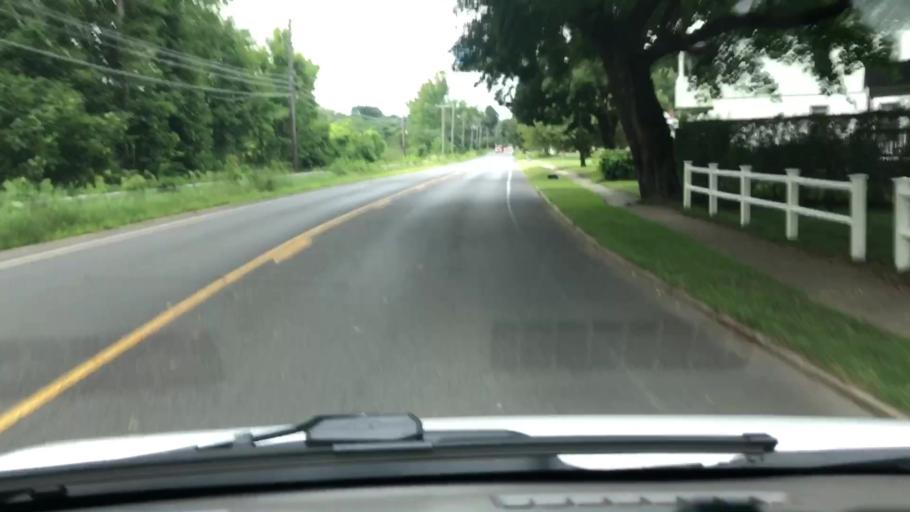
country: US
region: Massachusetts
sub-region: Franklin County
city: Turners Falls
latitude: 42.5979
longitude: -72.5645
